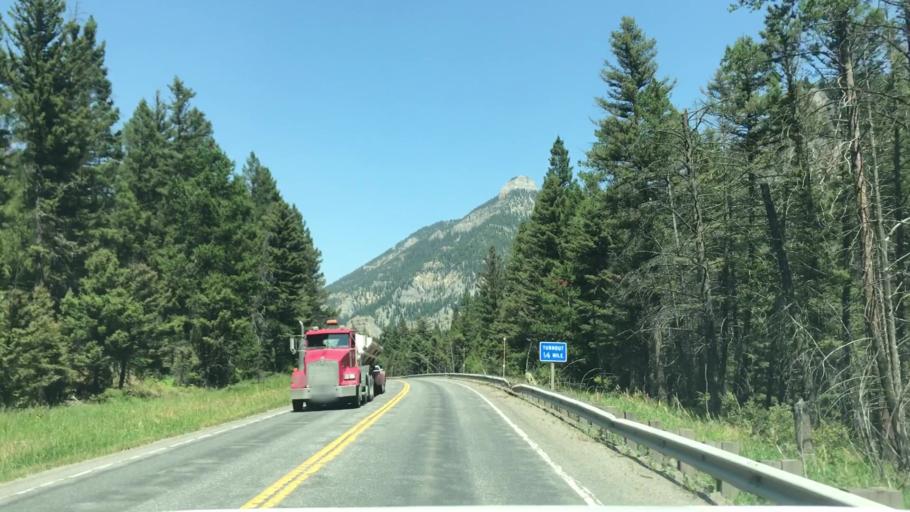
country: US
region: Montana
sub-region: Gallatin County
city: Big Sky
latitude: 45.4273
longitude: -111.2332
